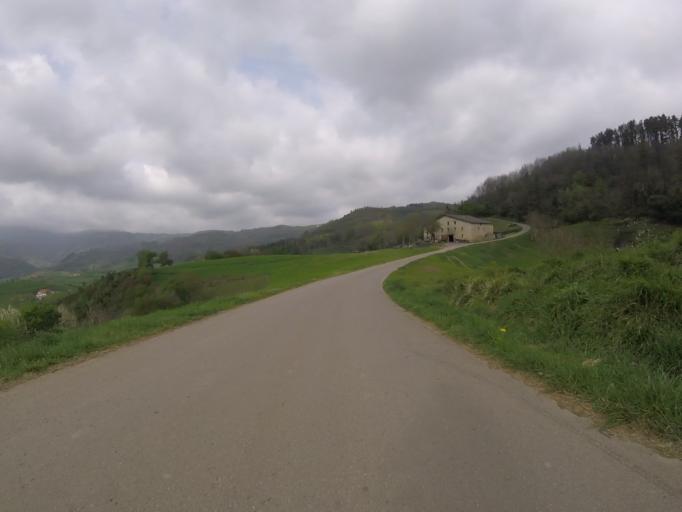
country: ES
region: Basque Country
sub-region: Provincia de Guipuzcoa
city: Zizurkil
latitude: 43.2099
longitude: -2.0811
